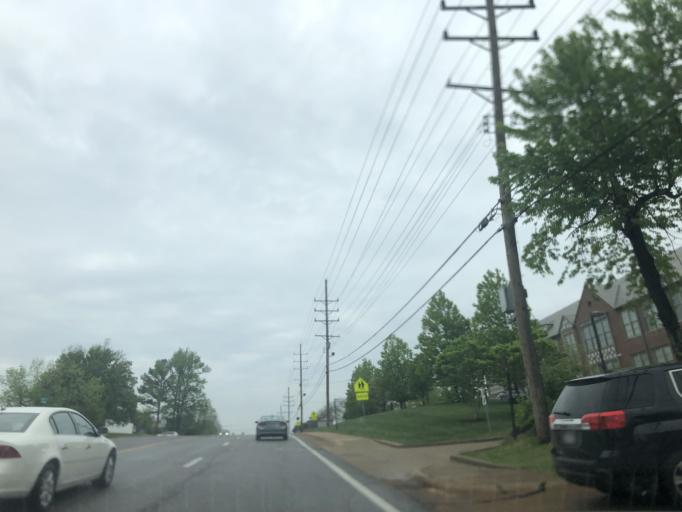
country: US
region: Missouri
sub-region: Saint Louis County
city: Affton
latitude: 38.5566
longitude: -90.3224
